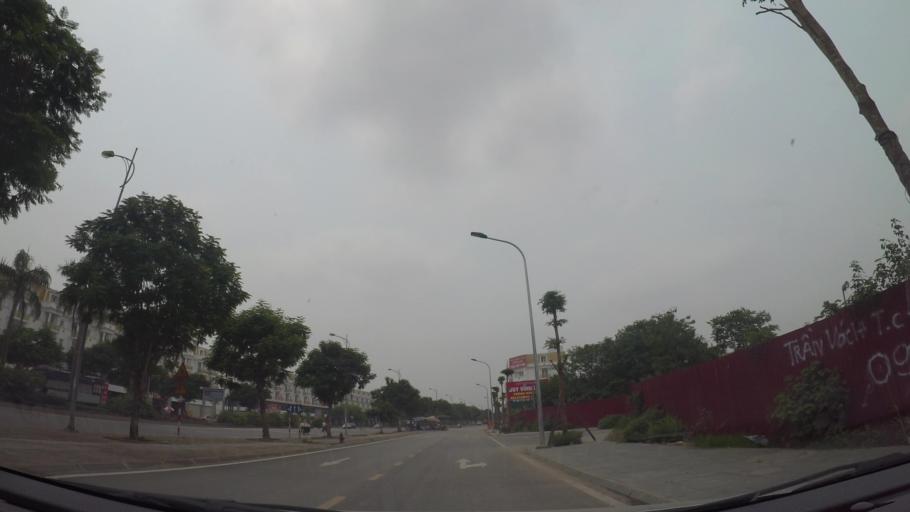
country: VN
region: Ha Noi
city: Ha Dong
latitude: 20.9833
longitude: 105.7414
